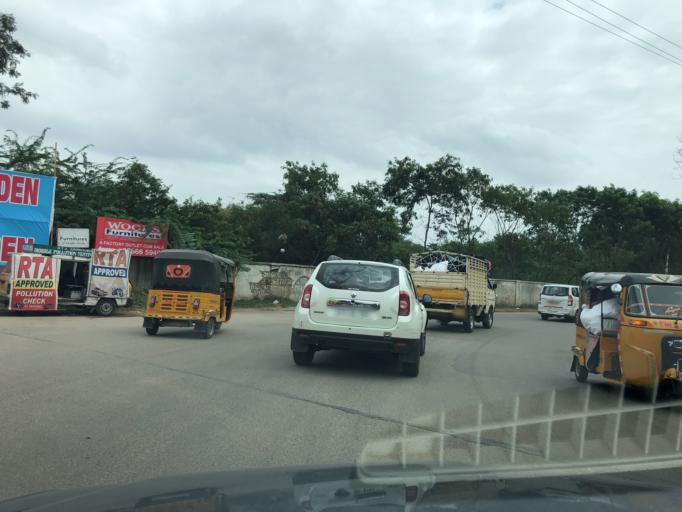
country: IN
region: Telangana
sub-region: Rangareddi
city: Quthbullapur
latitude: 17.4708
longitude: 78.4764
